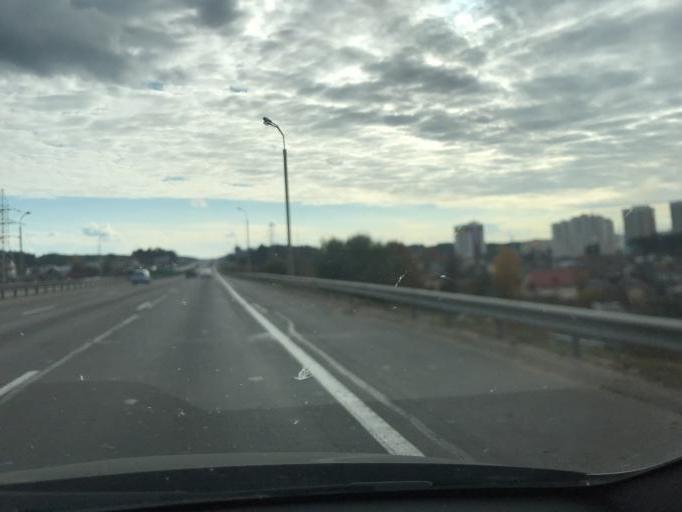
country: BY
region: Minsk
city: Vyaliki Trastsyanets
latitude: 53.9207
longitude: 27.6812
